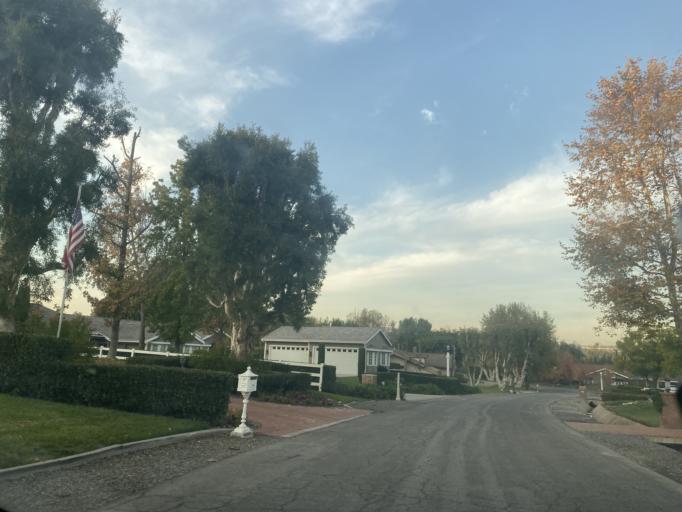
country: US
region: California
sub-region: Orange County
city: North Tustin
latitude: 33.7979
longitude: -117.7798
